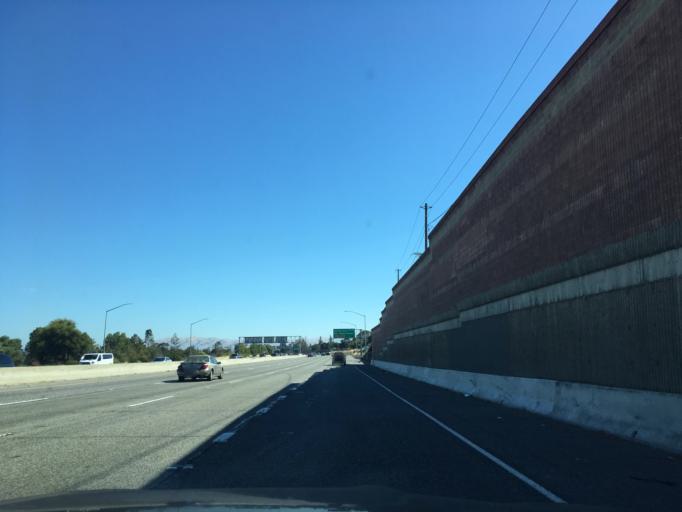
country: US
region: California
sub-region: Santa Clara County
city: Cambrian Park
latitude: 37.2603
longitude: -121.9523
